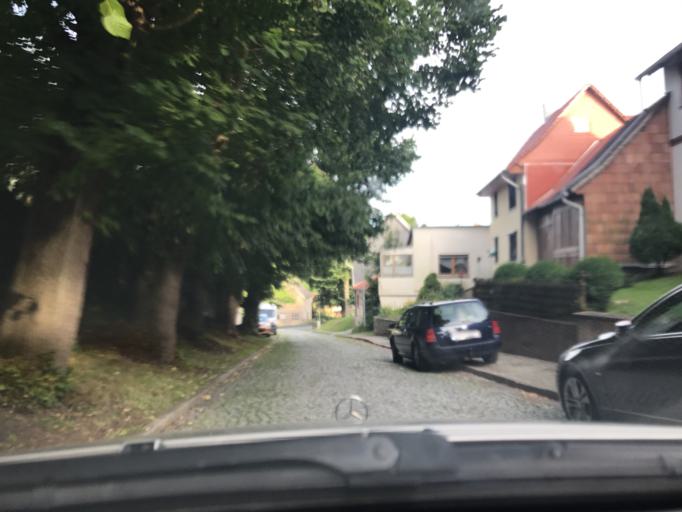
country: DE
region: Thuringia
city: Anrode
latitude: 51.2380
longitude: 10.3645
